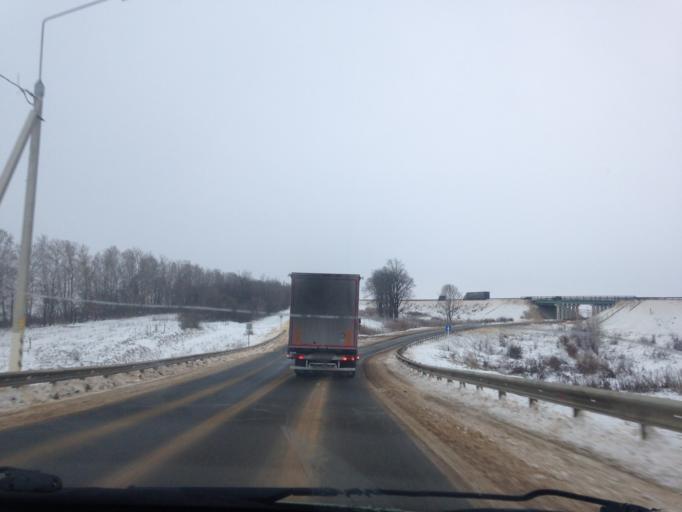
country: RU
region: Tula
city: Shchekino
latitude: 53.9493
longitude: 37.4893
